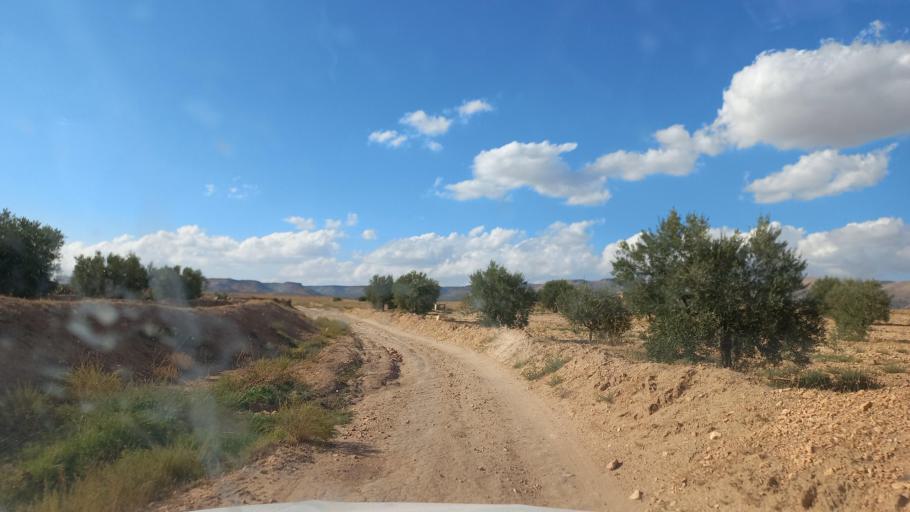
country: TN
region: Al Qasrayn
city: Sbiba
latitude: 35.3963
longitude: 9.0337
